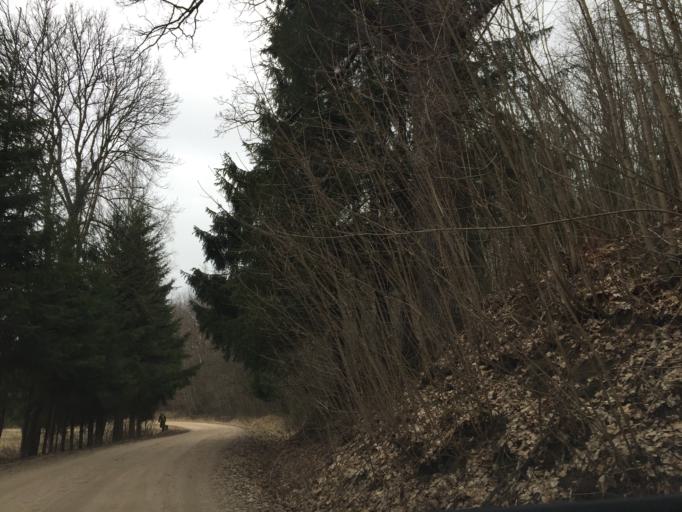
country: LV
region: Kraslavas Rajons
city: Kraslava
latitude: 55.9800
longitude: 27.1611
